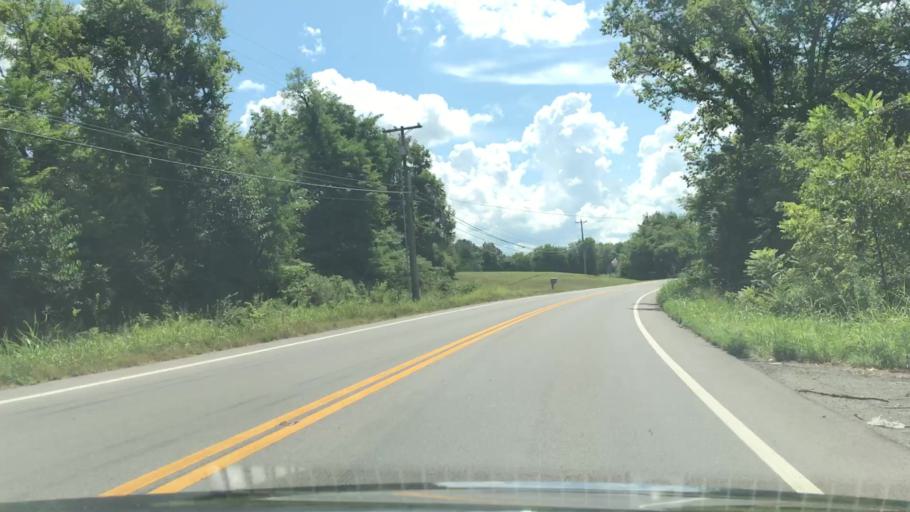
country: US
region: Tennessee
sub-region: Williamson County
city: Franklin
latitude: 35.9029
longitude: -86.7901
